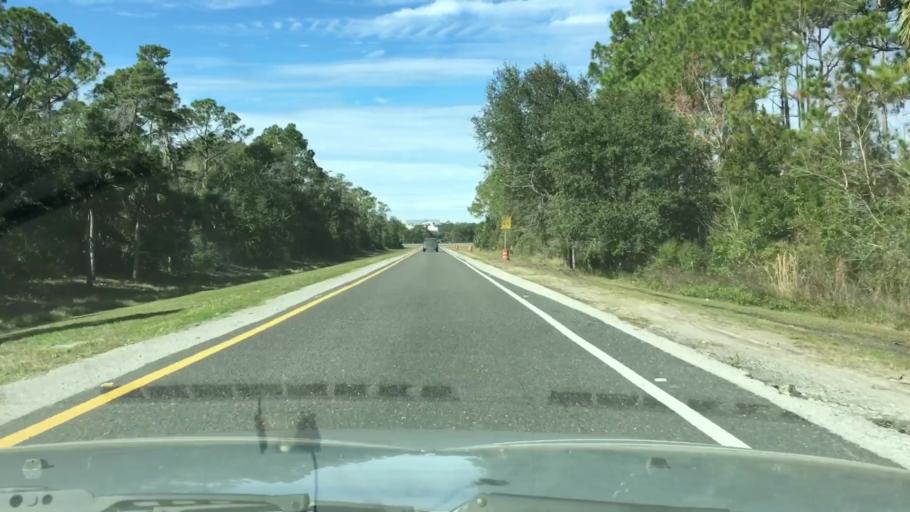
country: US
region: Florida
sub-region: Flagler County
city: Palm Coast
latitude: 29.5552
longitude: -81.2166
